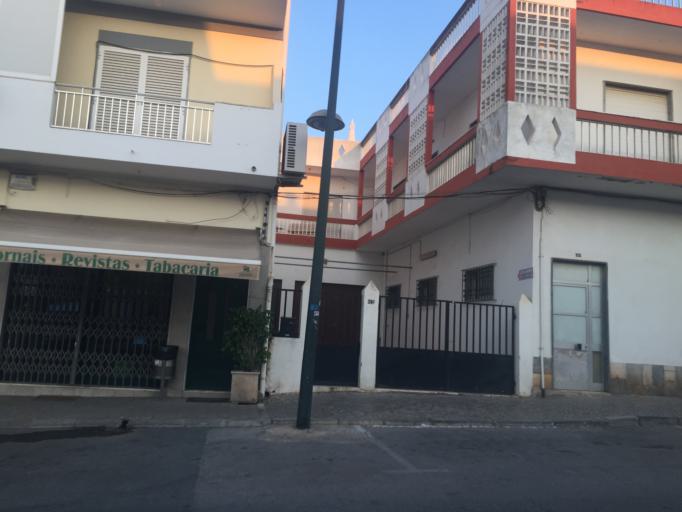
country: PT
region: Faro
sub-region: Faro
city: Faro
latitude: 37.0344
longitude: -7.9606
